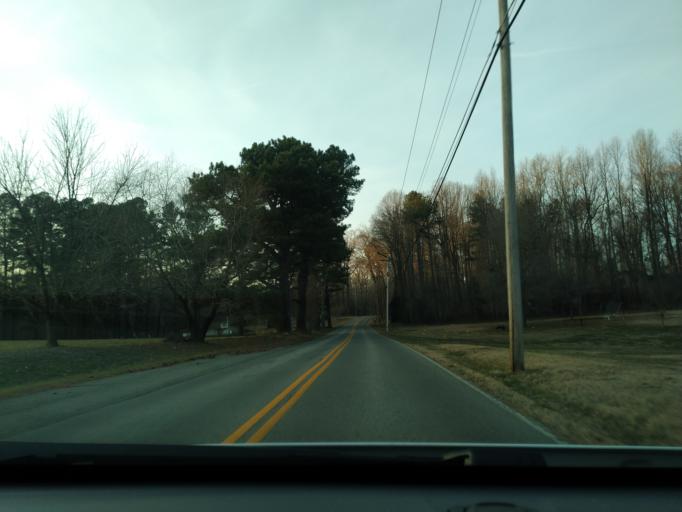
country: US
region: Maryland
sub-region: Calvert County
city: Huntingtown
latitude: 38.6003
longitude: -76.5684
